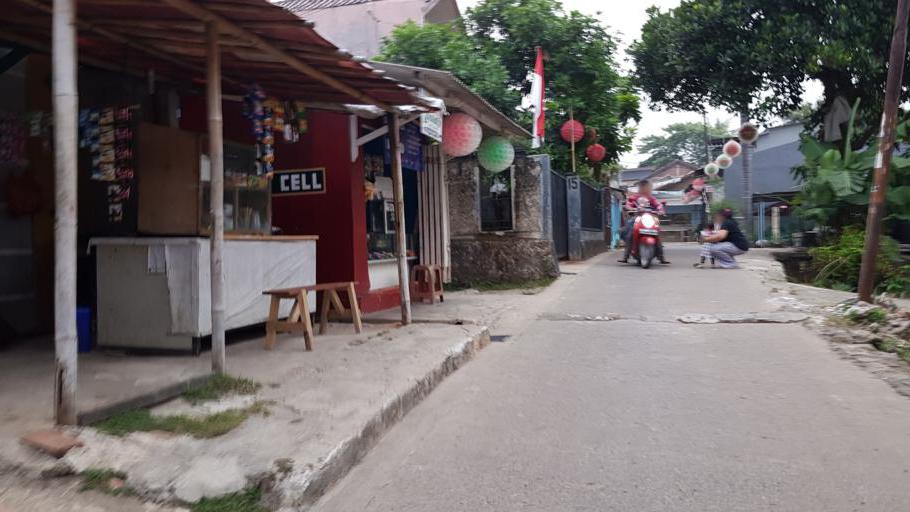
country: ID
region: West Java
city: Sawangan
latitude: -6.3979
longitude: 106.7694
